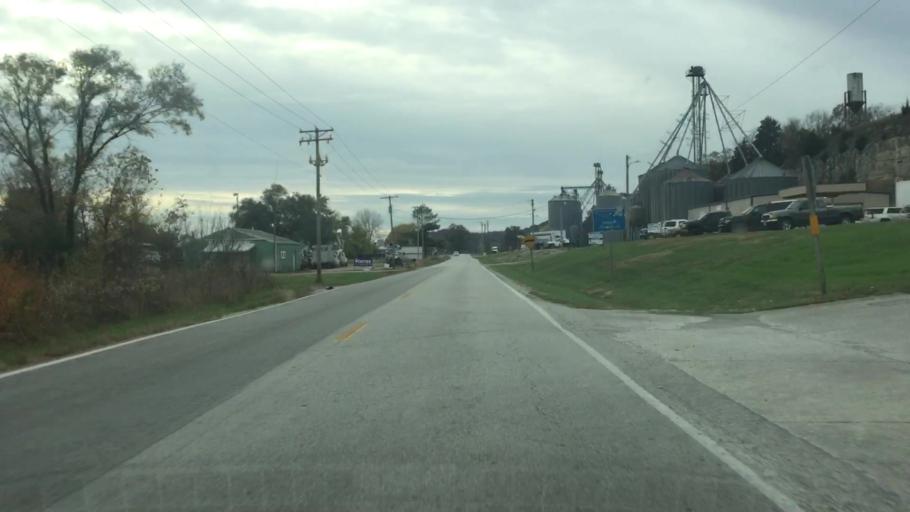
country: US
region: Missouri
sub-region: Gasconade County
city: Hermann
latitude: 38.7195
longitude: -91.5126
